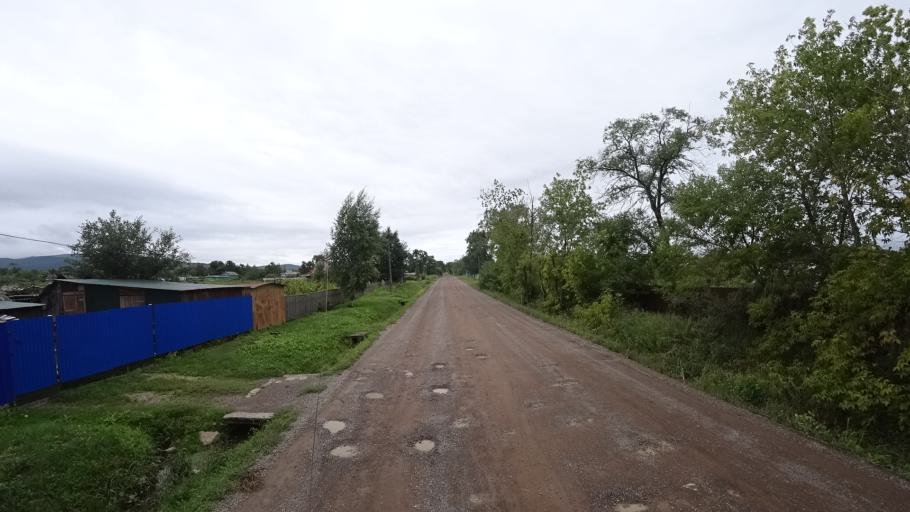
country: RU
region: Primorskiy
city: Chernigovka
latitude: 44.3412
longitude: 132.5690
